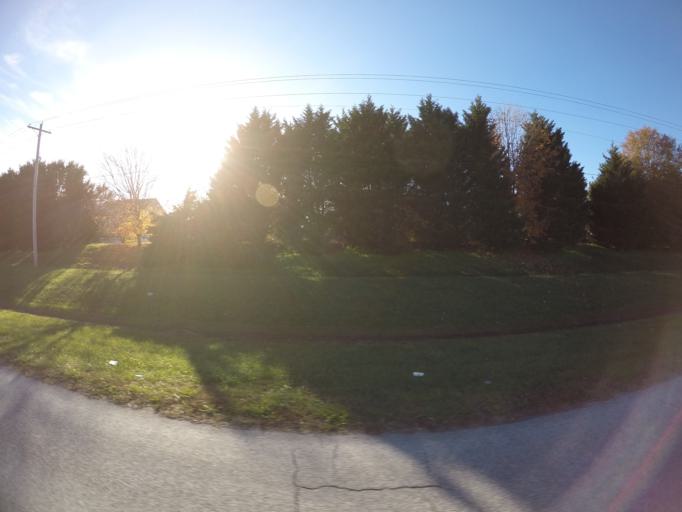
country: US
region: Maryland
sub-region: Saint Mary's County
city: Leonardtown
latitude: 38.3176
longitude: -76.6694
